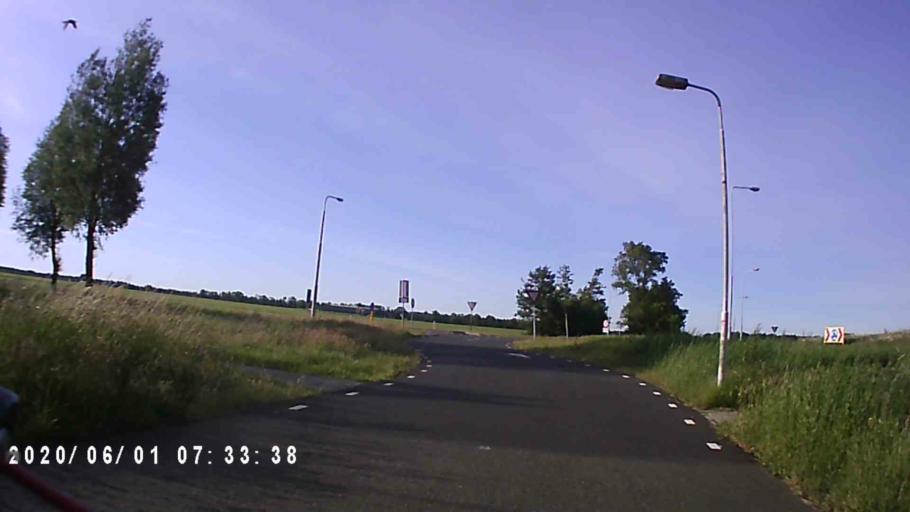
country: NL
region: Friesland
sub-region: Gemeente Dongeradeel
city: Dokkum
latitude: 53.3111
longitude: 5.9940
